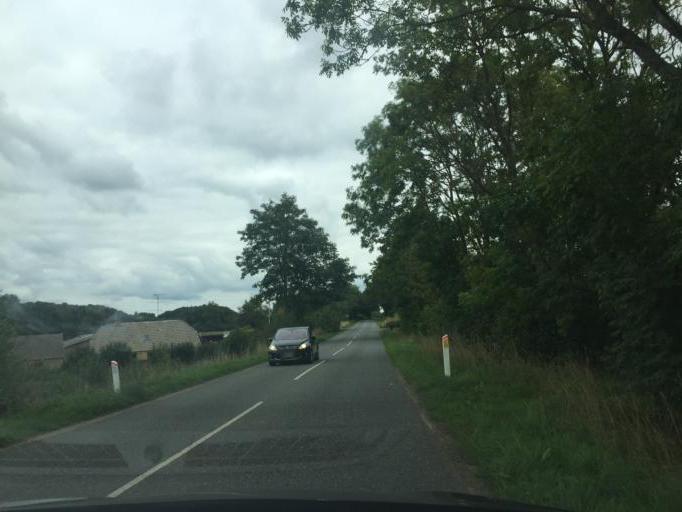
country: DK
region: South Denmark
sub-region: Assens Kommune
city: Tommerup
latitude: 55.3554
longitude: 10.2214
